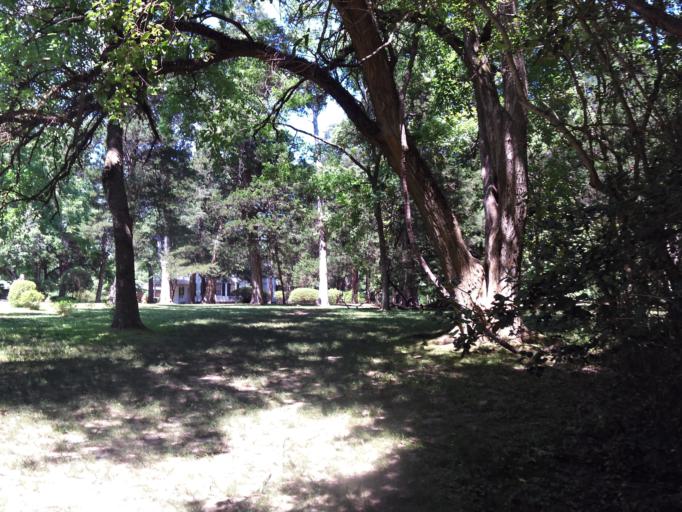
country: US
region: Mississippi
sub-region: Lafayette County
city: University
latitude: 34.3591
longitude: -89.5254
